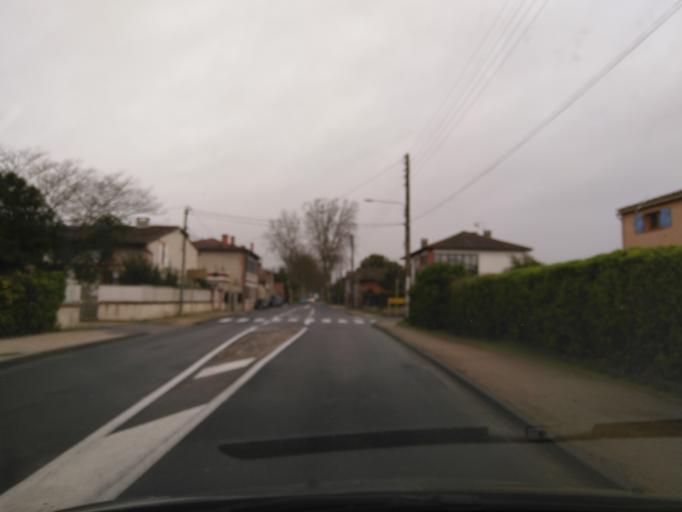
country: FR
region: Midi-Pyrenees
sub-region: Departement de la Haute-Garonne
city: Carbonne
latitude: 43.2977
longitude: 1.2193
